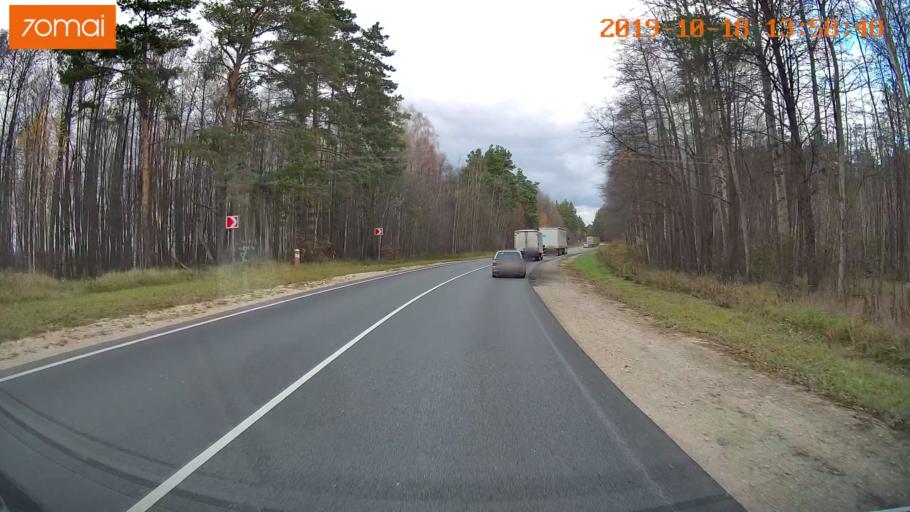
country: RU
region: Rjazan
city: Spas-Klepiki
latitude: 55.0885
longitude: 40.0571
